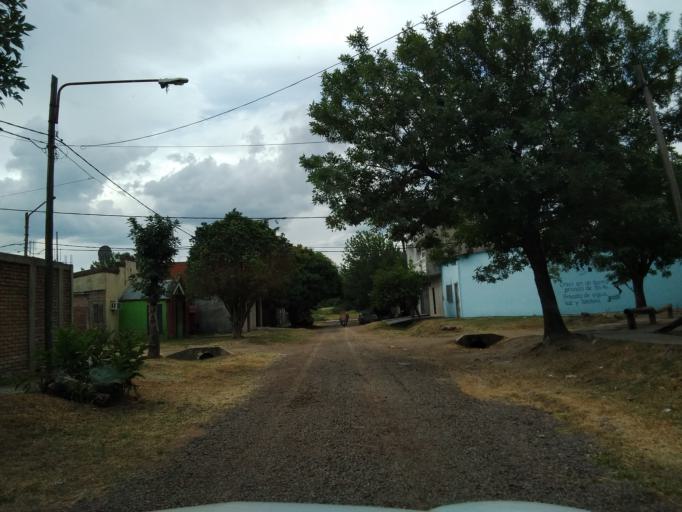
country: AR
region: Corrientes
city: Corrientes
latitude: -27.5185
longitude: -58.7903
